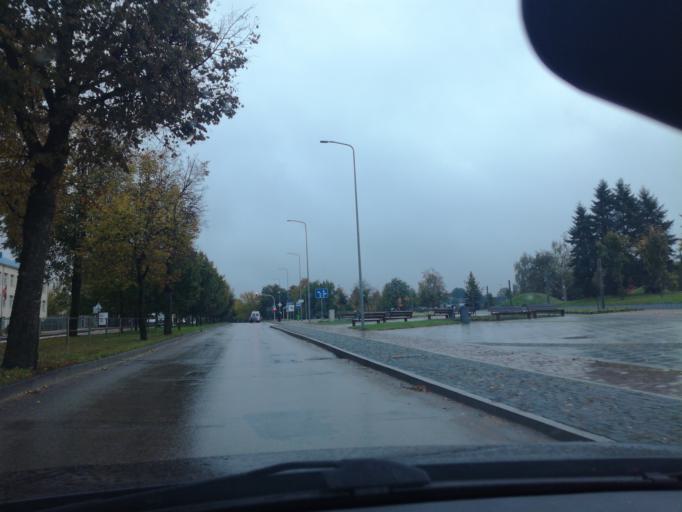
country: LT
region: Alytaus apskritis
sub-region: Alytus
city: Alytus
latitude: 54.4030
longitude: 24.0633
